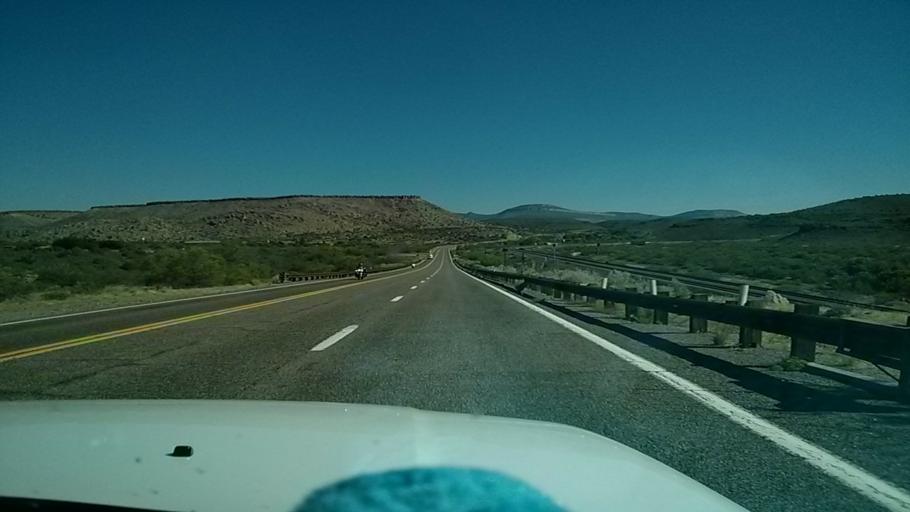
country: US
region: Arizona
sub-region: Mohave County
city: Peach Springs
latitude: 35.4178
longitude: -113.6471
